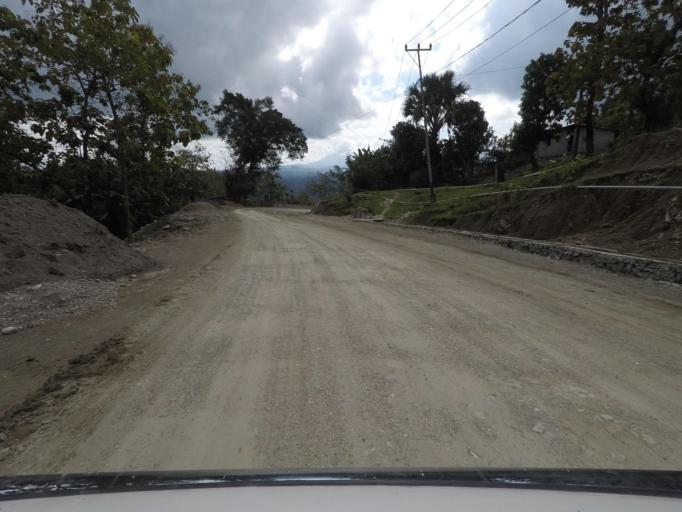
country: TL
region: Viqueque
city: Viqueque
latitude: -8.7895
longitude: 126.3763
